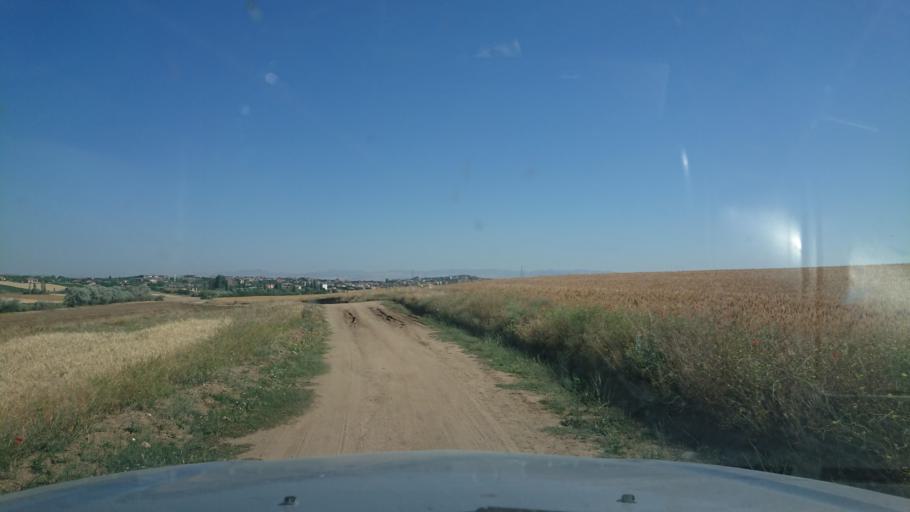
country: TR
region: Aksaray
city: Agacoren
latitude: 38.8536
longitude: 33.9146
